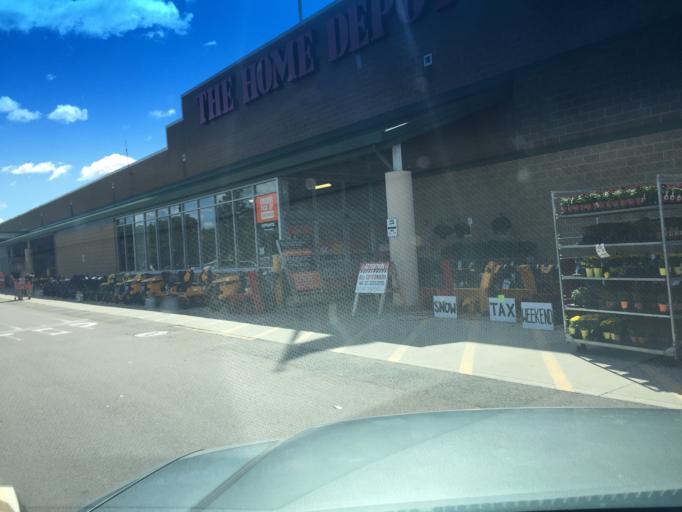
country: US
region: Massachusetts
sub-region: Norfolk County
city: Bellingham
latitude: 42.1119
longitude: -71.4692
